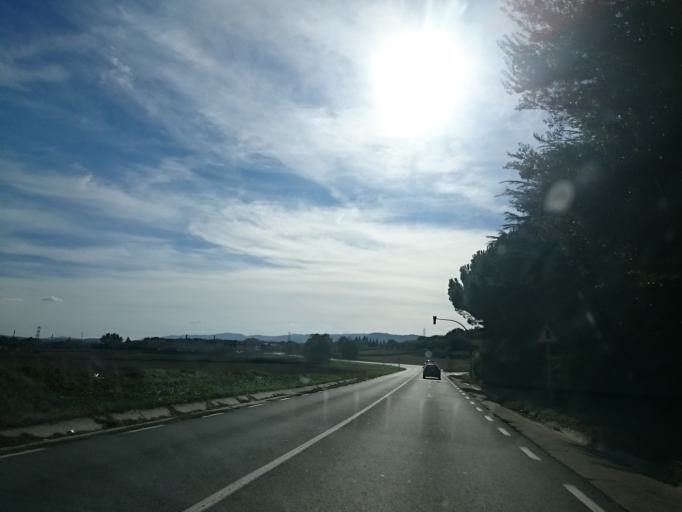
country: ES
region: Catalonia
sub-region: Provincia de Barcelona
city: Vic
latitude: 41.9421
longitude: 2.2696
